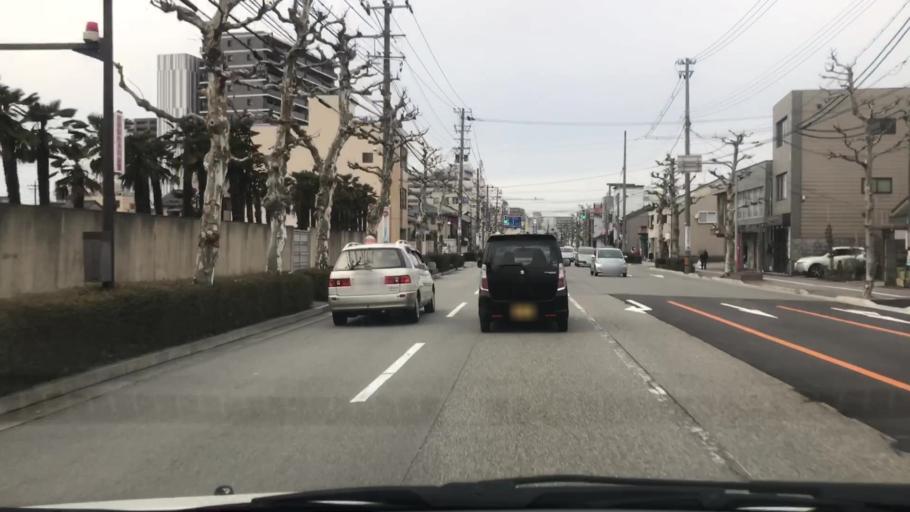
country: JP
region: Toyama
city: Toyama-shi
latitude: 36.6865
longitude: 137.2217
